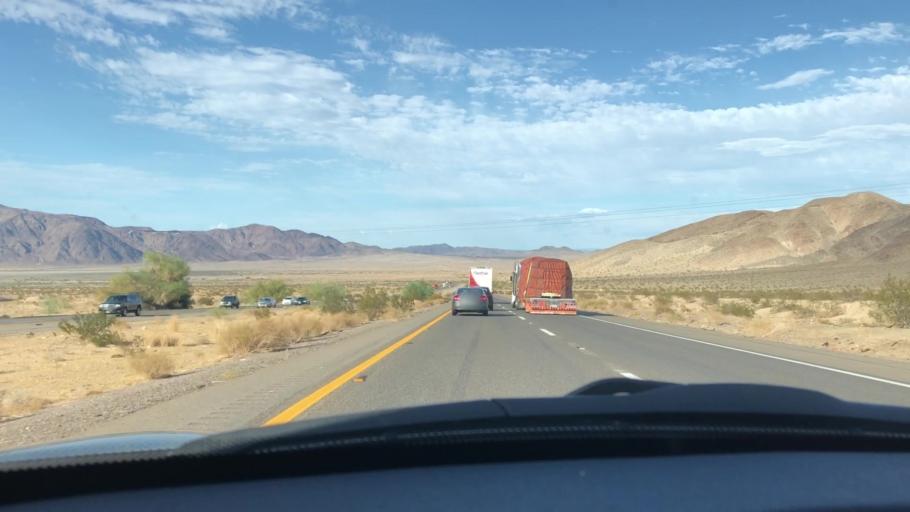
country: US
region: California
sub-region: San Bernardino County
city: Fort Irwin
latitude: 35.0907
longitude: -116.3114
